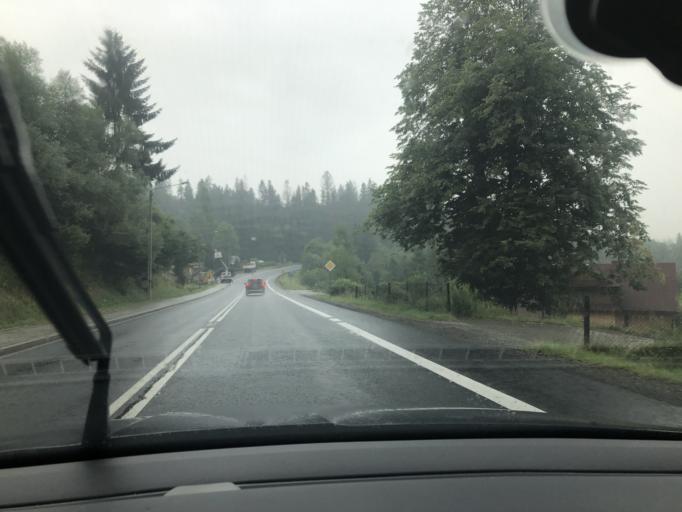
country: PL
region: Lesser Poland Voivodeship
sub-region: Powiat nowotarski
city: Jablonka
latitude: 49.5073
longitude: 19.7169
